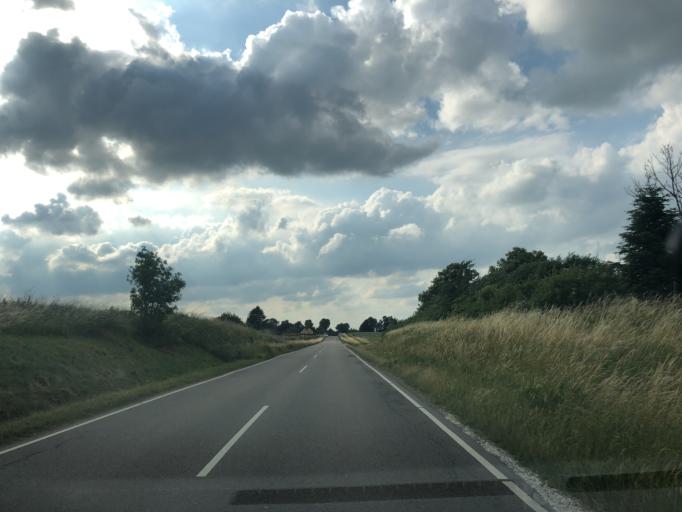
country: DK
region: Zealand
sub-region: Faxe Kommune
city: Haslev
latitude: 55.3134
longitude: 11.9851
